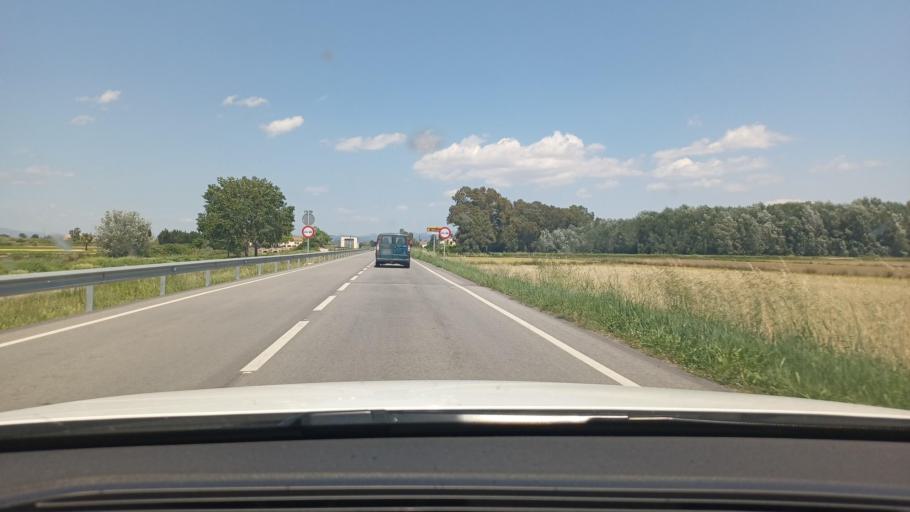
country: ES
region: Catalonia
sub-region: Provincia de Tarragona
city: Amposta
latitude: 40.6682
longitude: 0.5907
